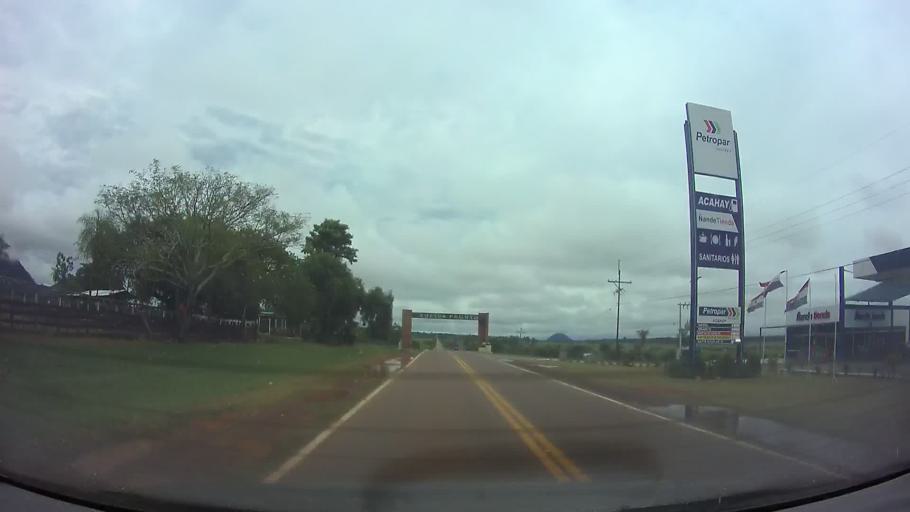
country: PY
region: Paraguari
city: Acahay
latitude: -25.8996
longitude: -57.1170
